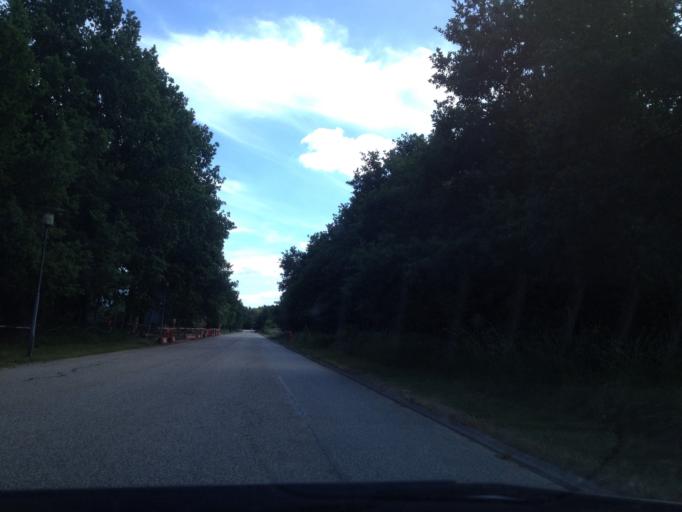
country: DK
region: Capital Region
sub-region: Horsholm Kommune
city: Horsholm
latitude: 55.8724
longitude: 12.4927
